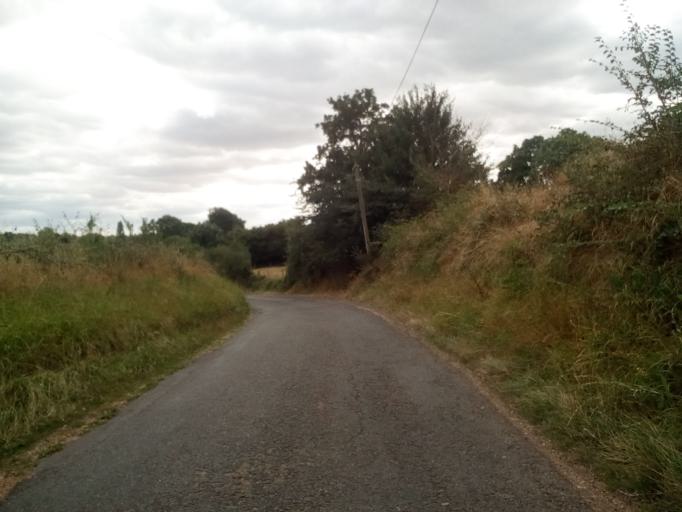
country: FR
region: Lower Normandy
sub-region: Departement du Calvados
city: Troarn
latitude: 49.1627
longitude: -0.1533
